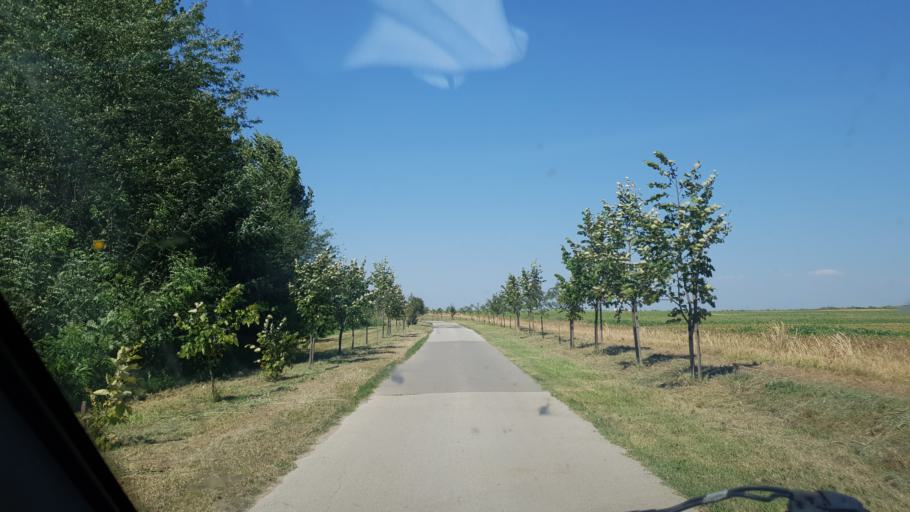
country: RS
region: Autonomna Pokrajina Vojvodina
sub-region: Juznobacki Okrug
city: Kovilj
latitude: 45.2046
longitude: 20.0639
